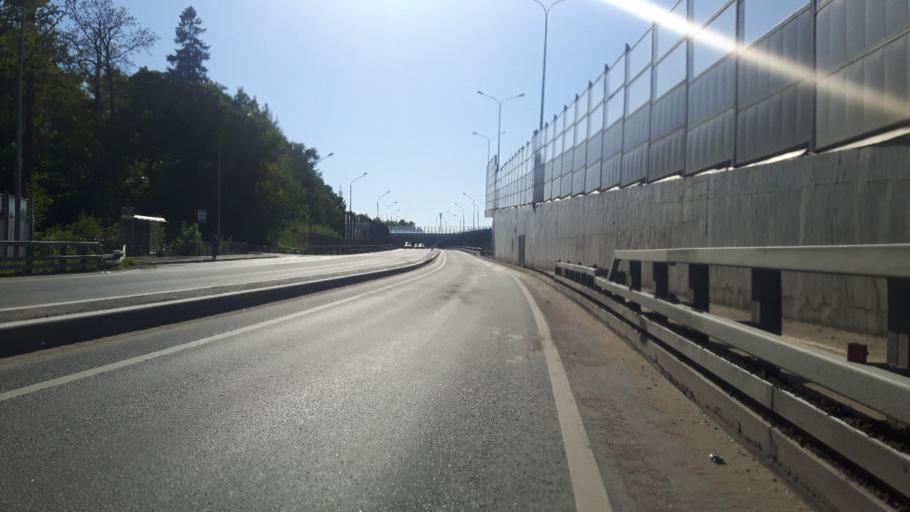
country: RU
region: St.-Petersburg
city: Lomonosov
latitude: 59.9265
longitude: 29.6759
